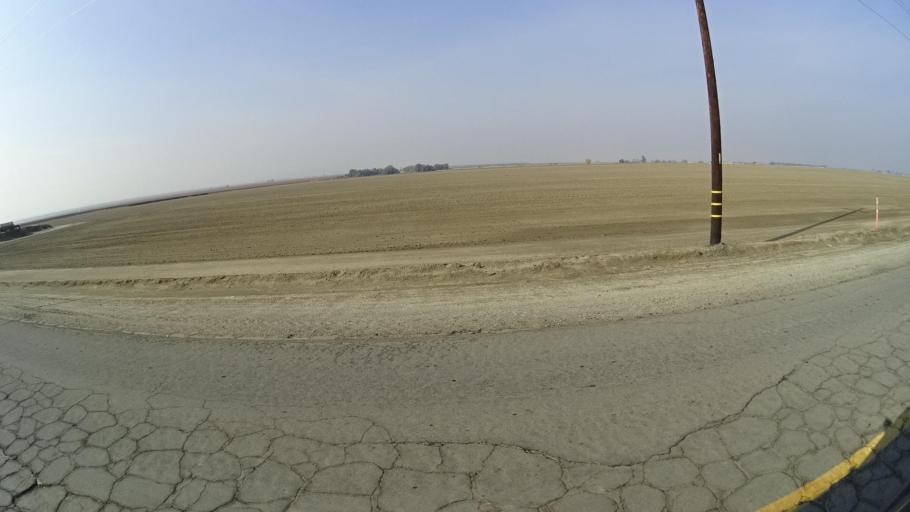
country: US
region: California
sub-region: Kern County
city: Arvin
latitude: 35.0475
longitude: -118.8466
